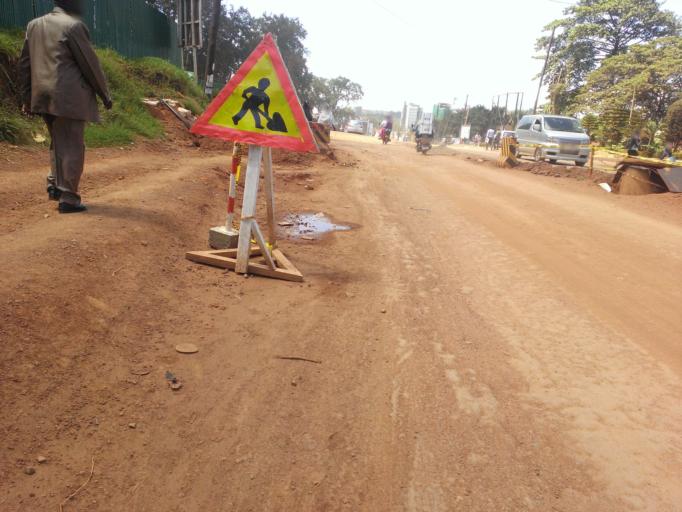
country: UG
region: Central Region
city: Kampala Central Division
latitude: 0.3285
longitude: 32.5708
